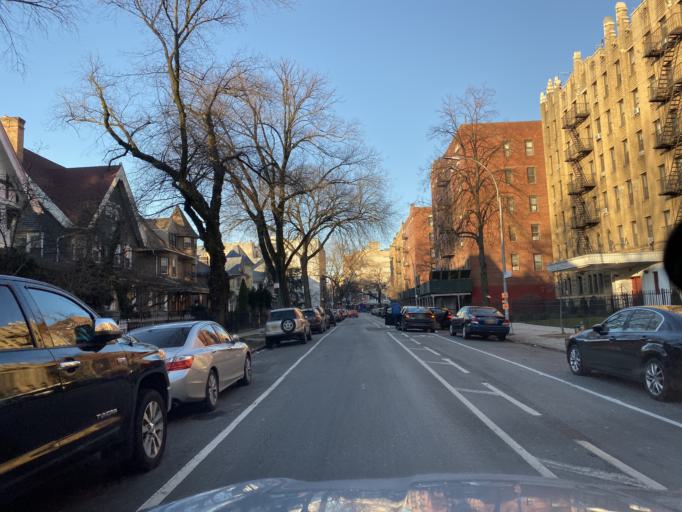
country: US
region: New York
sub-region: Kings County
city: Brooklyn
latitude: 40.6611
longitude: -73.9585
